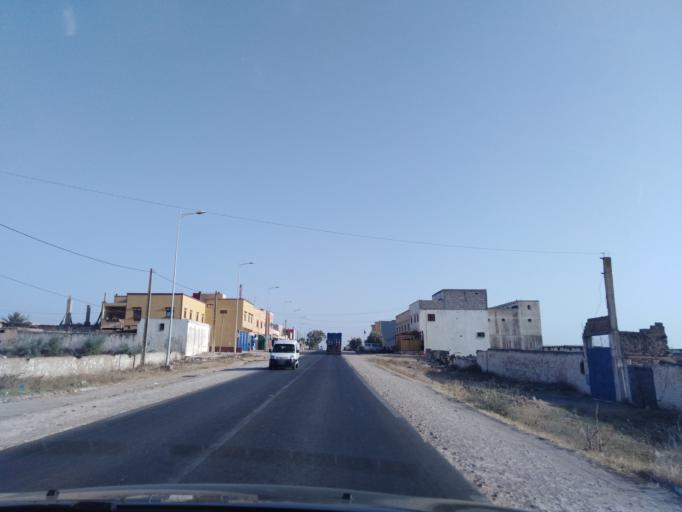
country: MA
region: Doukkala-Abda
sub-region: El-Jadida
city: Sidi Bennour
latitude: 32.5509
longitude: -8.7249
